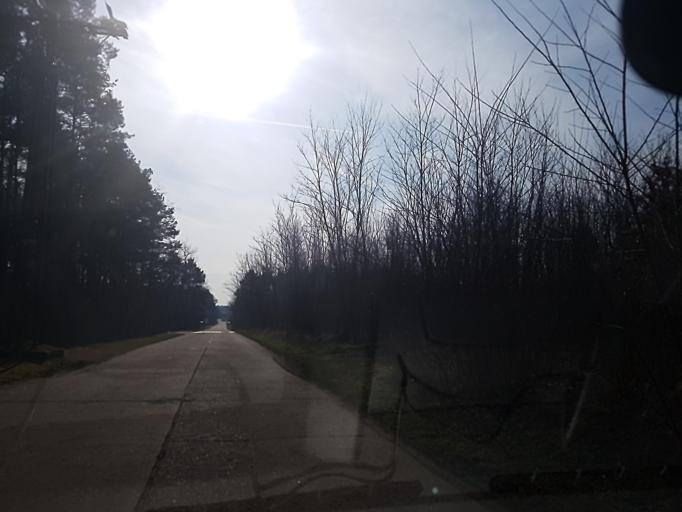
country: DE
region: Brandenburg
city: Wenzlow
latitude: 52.3311
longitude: 12.4397
